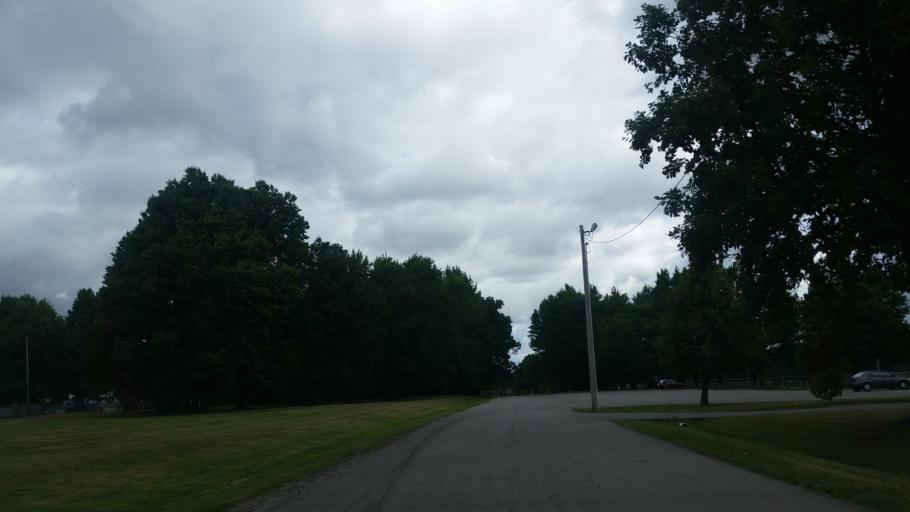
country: US
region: Ohio
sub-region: Cuyahoga County
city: Parma Heights
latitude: 41.3650
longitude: -81.7746
